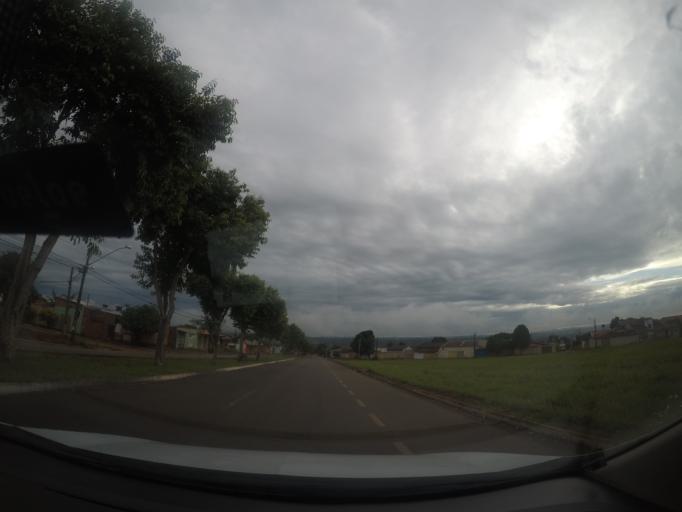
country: BR
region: Goias
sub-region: Goiania
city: Goiania
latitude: -16.6032
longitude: -49.3077
